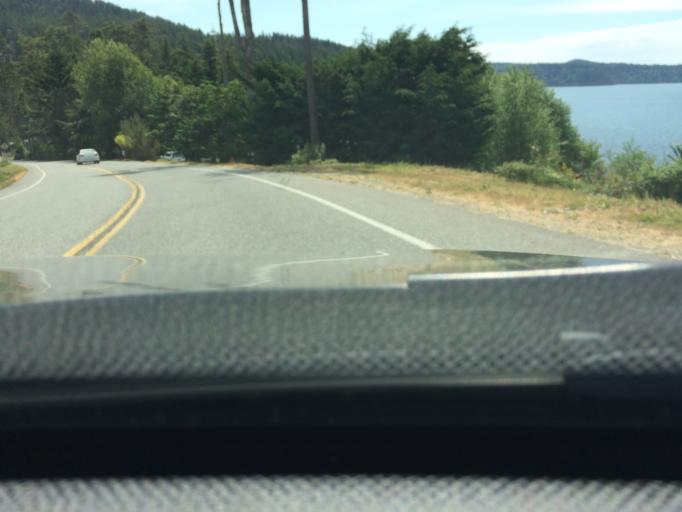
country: US
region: Washington
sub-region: Skagit County
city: Anacortes
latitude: 48.4881
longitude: -122.6699
